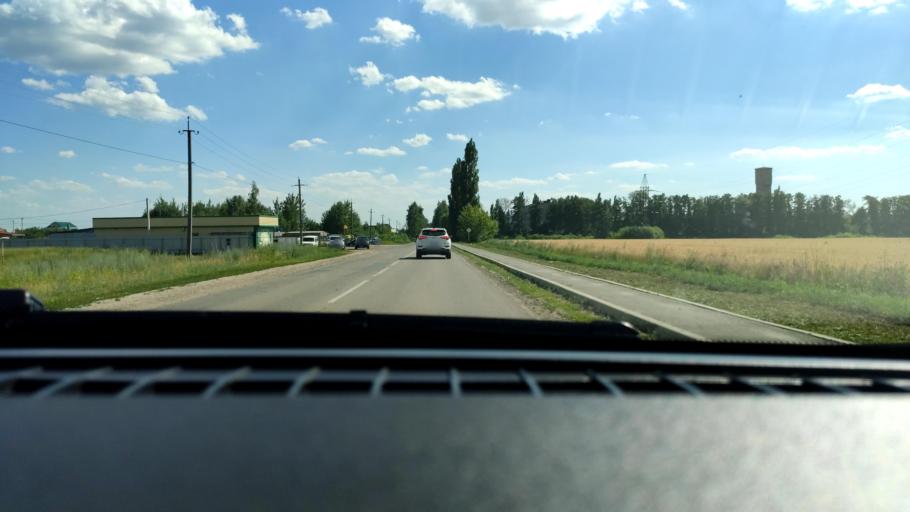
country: RU
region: Voronezj
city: Ramon'
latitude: 51.9445
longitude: 39.3531
